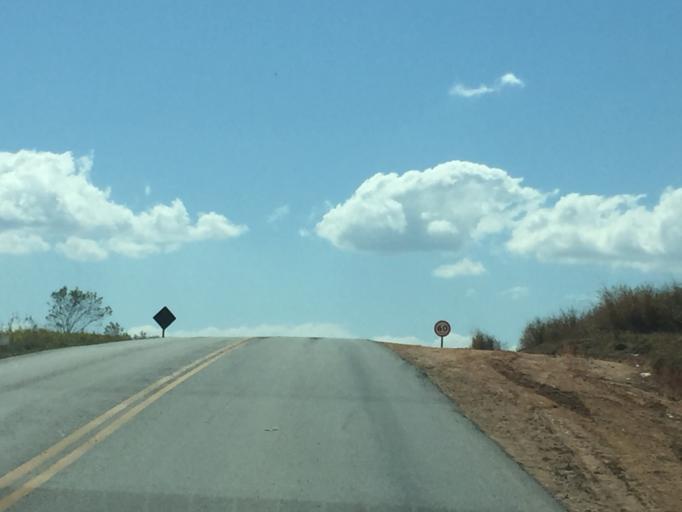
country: BR
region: Sao Paulo
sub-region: Moji-Guacu
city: Mogi-Gaucu
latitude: -22.3721
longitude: -46.8755
